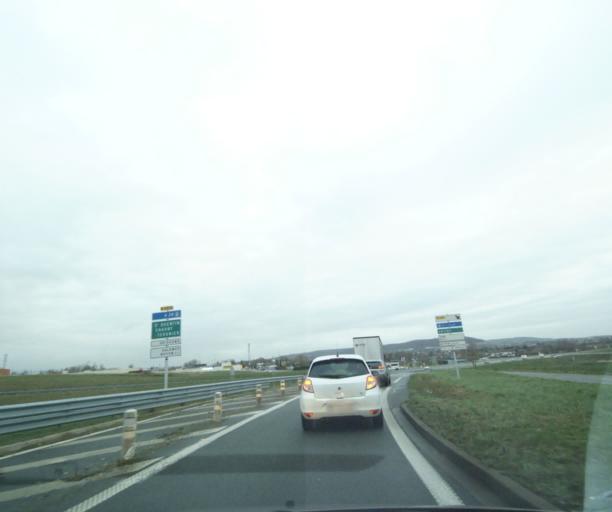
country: FR
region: Picardie
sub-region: Departement de l'Oise
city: Noyon
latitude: 49.5670
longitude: 2.9749
